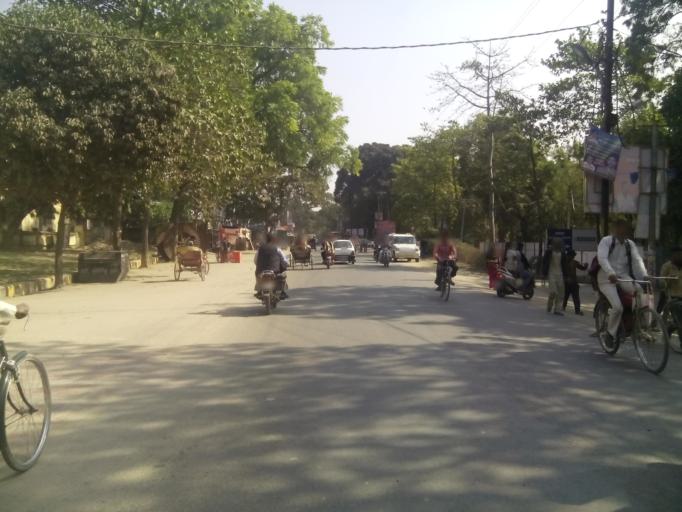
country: IN
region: Uttar Pradesh
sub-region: Bahraich
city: Bahraich
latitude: 27.5657
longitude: 81.5952
